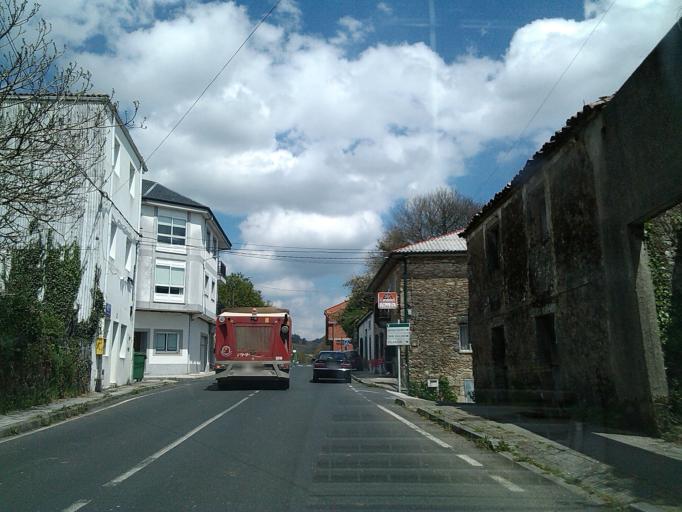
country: ES
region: Galicia
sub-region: Provincia da Coruna
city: Melide
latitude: 42.9667
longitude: -7.9731
